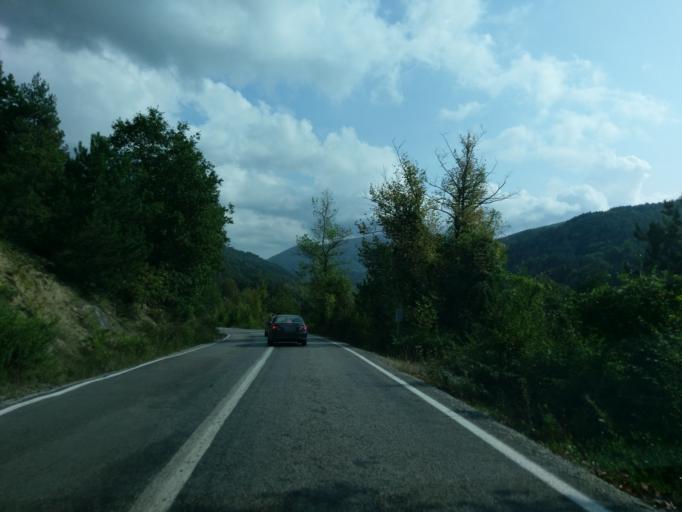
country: TR
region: Sinop
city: Yenikonak
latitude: 41.8745
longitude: 34.5465
